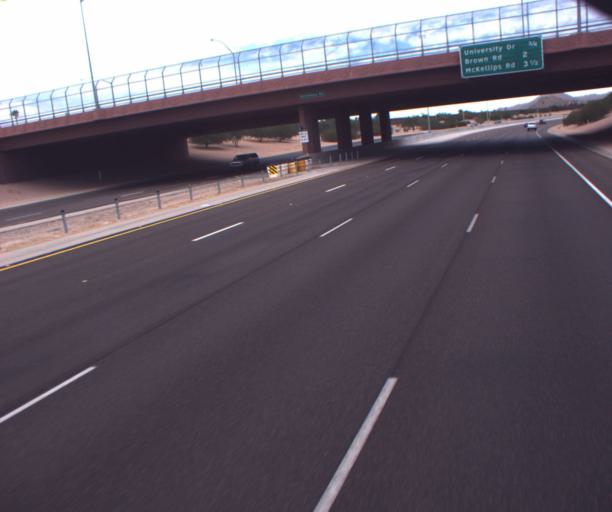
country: US
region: Arizona
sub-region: Pinal County
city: Apache Junction
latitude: 33.4072
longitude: -111.6401
